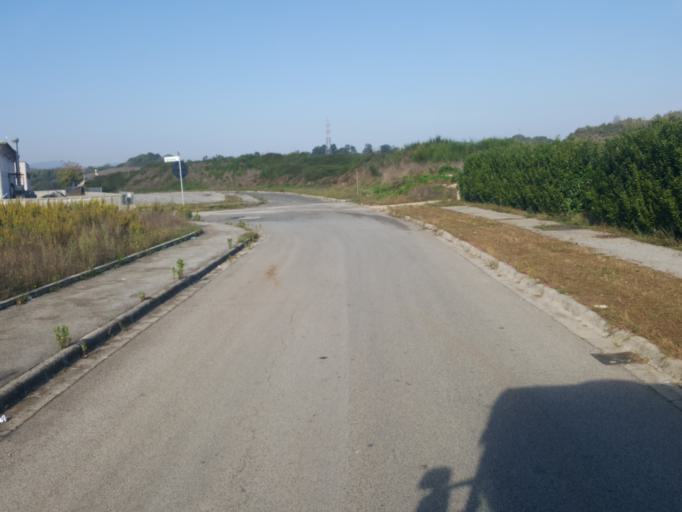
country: IT
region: Latium
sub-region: Citta metropolitana di Roma Capitale
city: Colleferro
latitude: 41.7575
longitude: 12.9914
